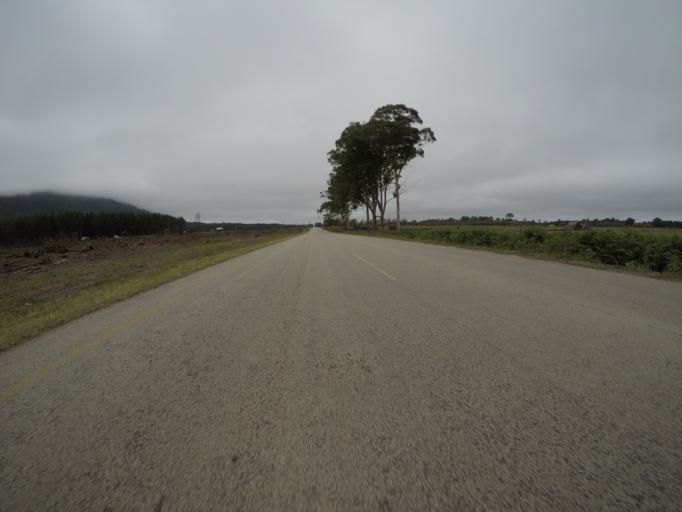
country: ZA
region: Eastern Cape
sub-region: Cacadu District Municipality
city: Kareedouw
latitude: -33.9842
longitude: 24.0606
